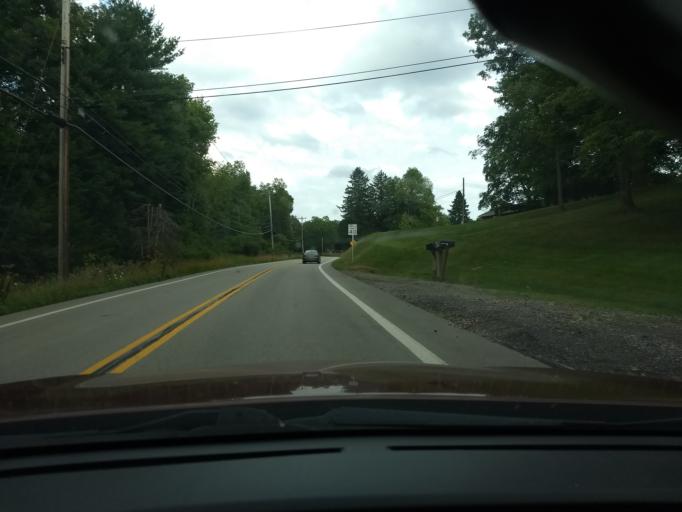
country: US
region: Pennsylvania
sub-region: Allegheny County
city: Bakerstown
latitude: 40.6543
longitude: -79.9027
